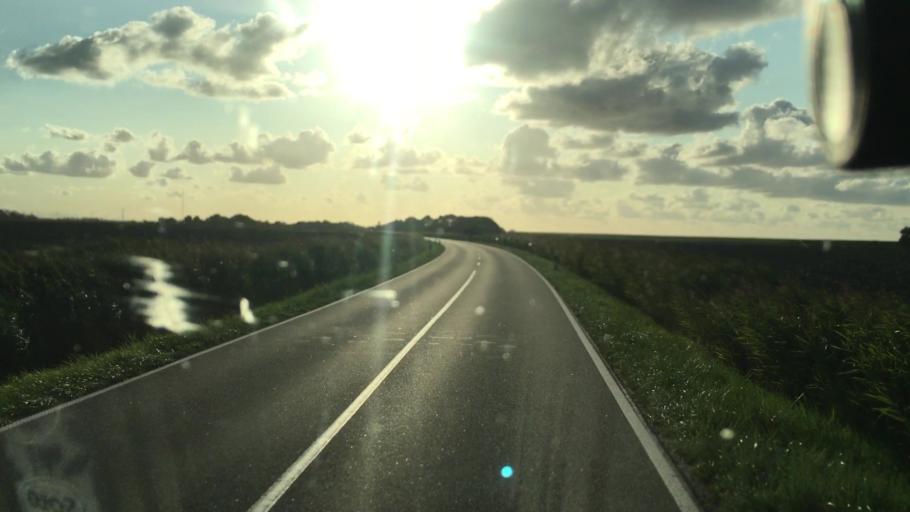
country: DE
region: Lower Saxony
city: Neuharlingersiel
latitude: 53.6898
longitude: 7.6828
